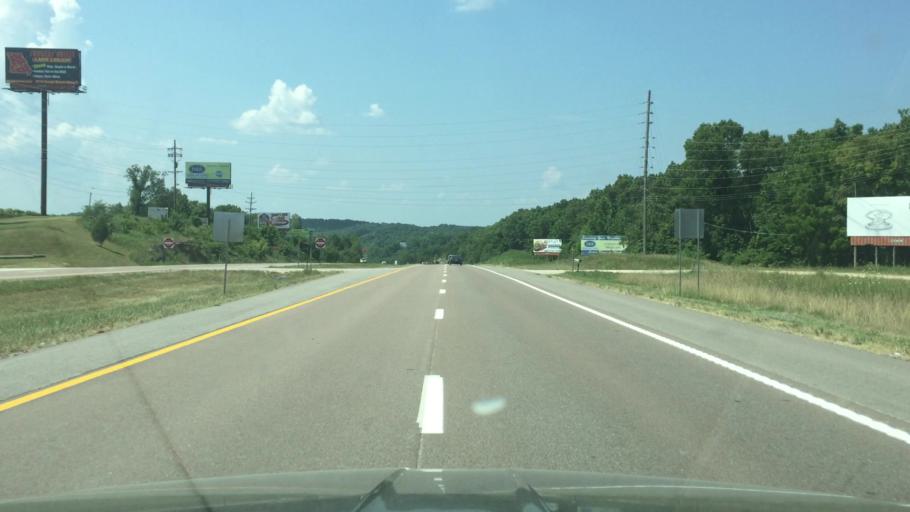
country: US
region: Missouri
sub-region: Miller County
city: Lake Ozark
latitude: 38.2578
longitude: -92.5862
